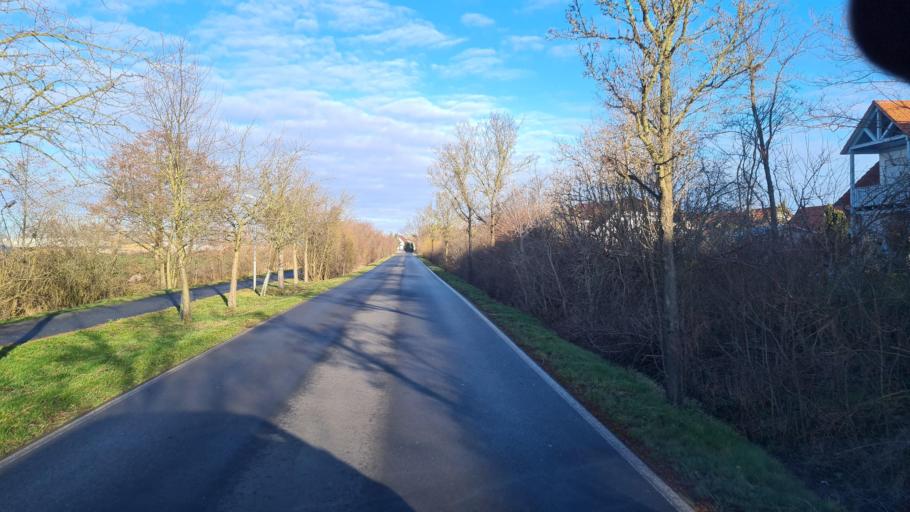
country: DE
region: Brandenburg
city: Herzberg
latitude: 51.6955
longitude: 13.2216
